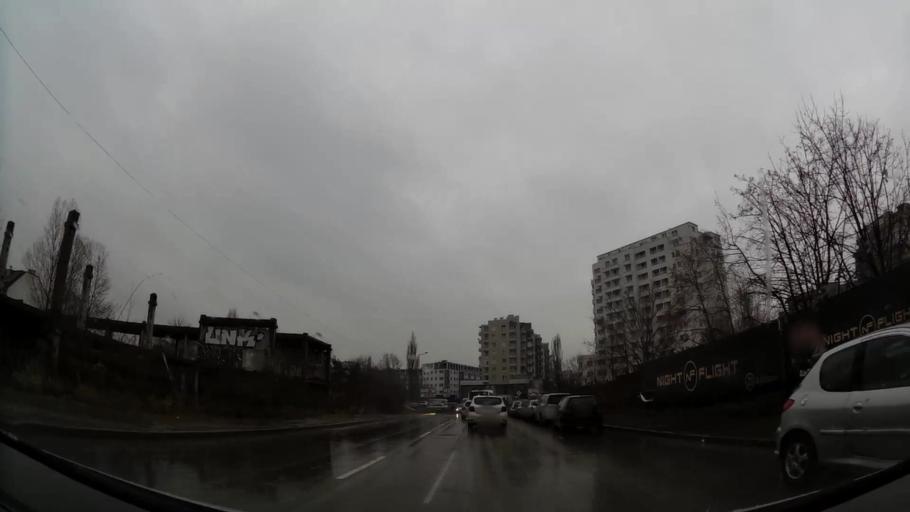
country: BG
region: Sofia-Capital
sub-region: Stolichna Obshtina
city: Sofia
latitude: 42.6469
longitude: 23.3419
